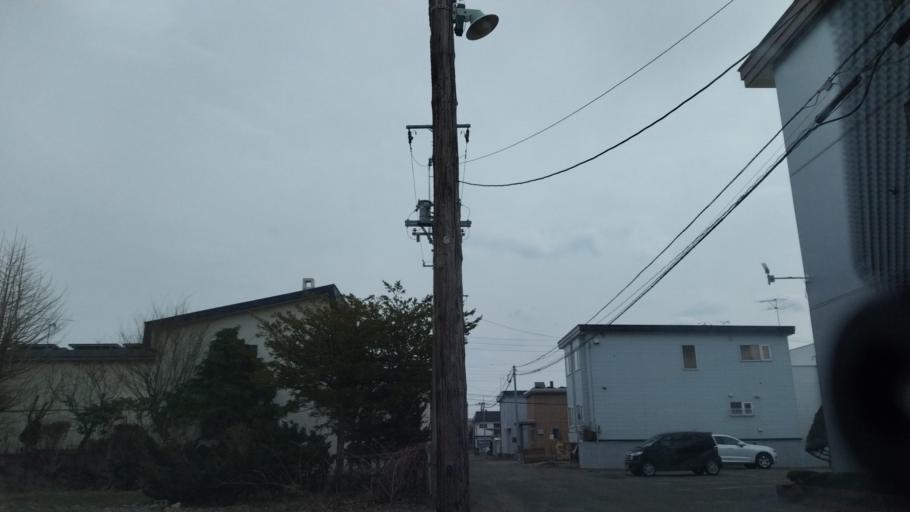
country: JP
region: Hokkaido
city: Obihiro
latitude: 42.9220
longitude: 143.2197
